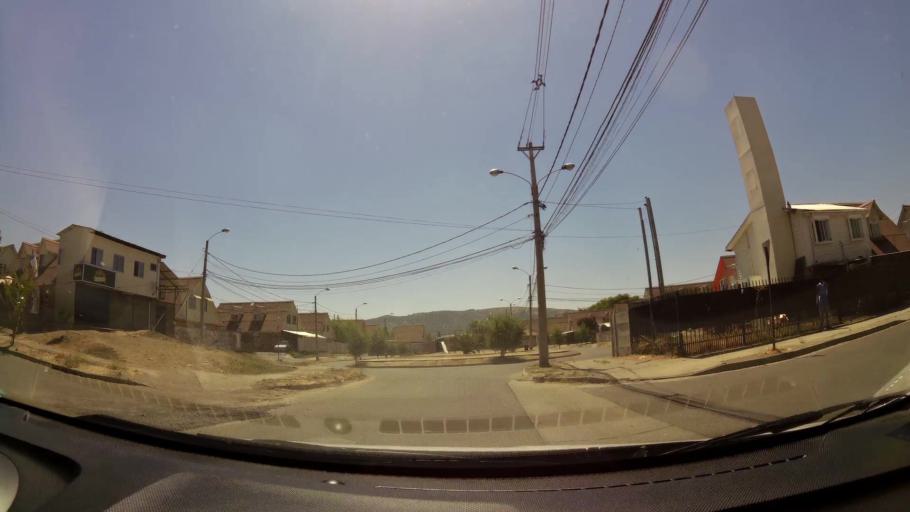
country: CL
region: Maule
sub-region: Provincia de Talca
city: Talca
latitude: -35.4011
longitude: -71.6426
